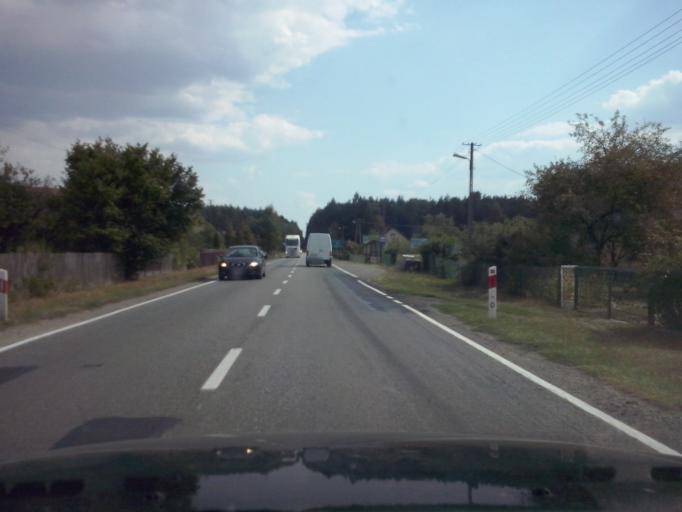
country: PL
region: Subcarpathian Voivodeship
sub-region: Powiat nizanski
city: Bieliny
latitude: 50.4005
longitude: 22.2943
